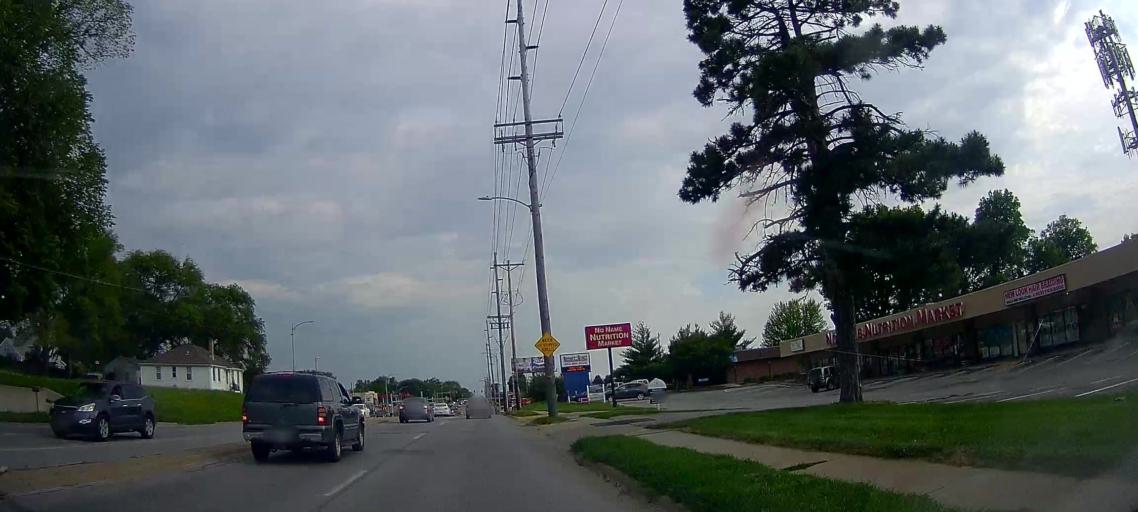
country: US
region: Nebraska
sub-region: Douglas County
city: Ralston
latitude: 41.2792
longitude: -96.0239
